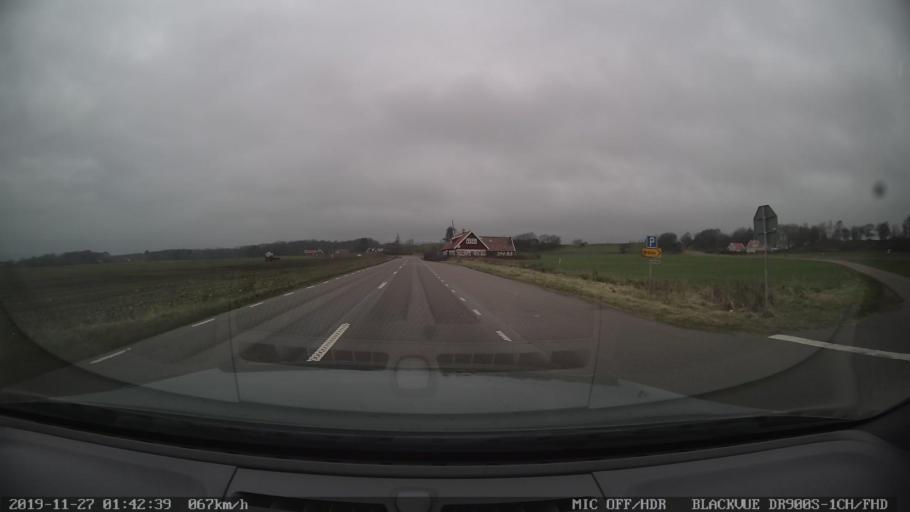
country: SE
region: Skane
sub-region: Hoganas Kommun
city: Hoganas
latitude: 56.2527
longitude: 12.5344
